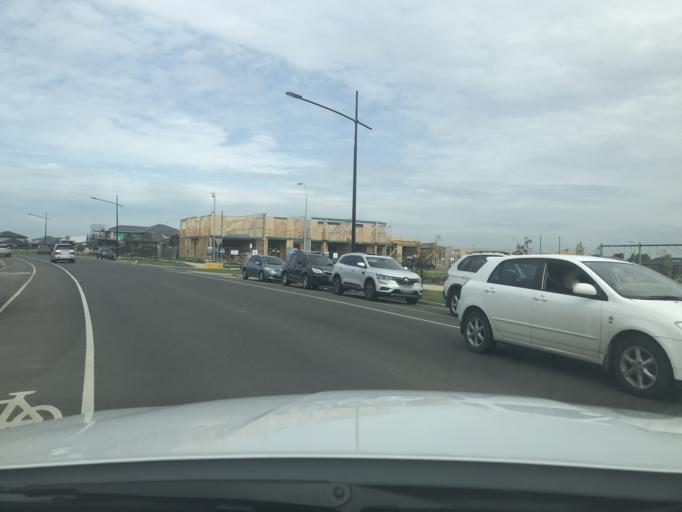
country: AU
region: Victoria
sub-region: Hume
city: Roxburgh Park
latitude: -37.6008
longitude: 144.8981
